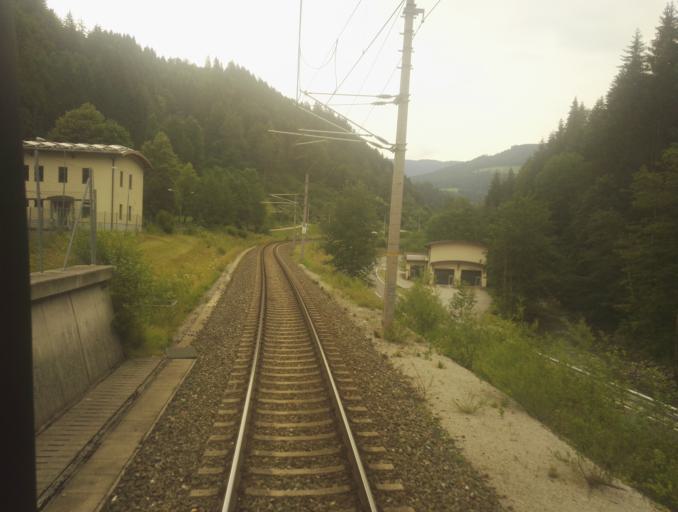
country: AT
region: Salzburg
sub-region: Politischer Bezirk Sankt Johann im Pongau
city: Huttau
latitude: 47.4217
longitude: 13.2963
